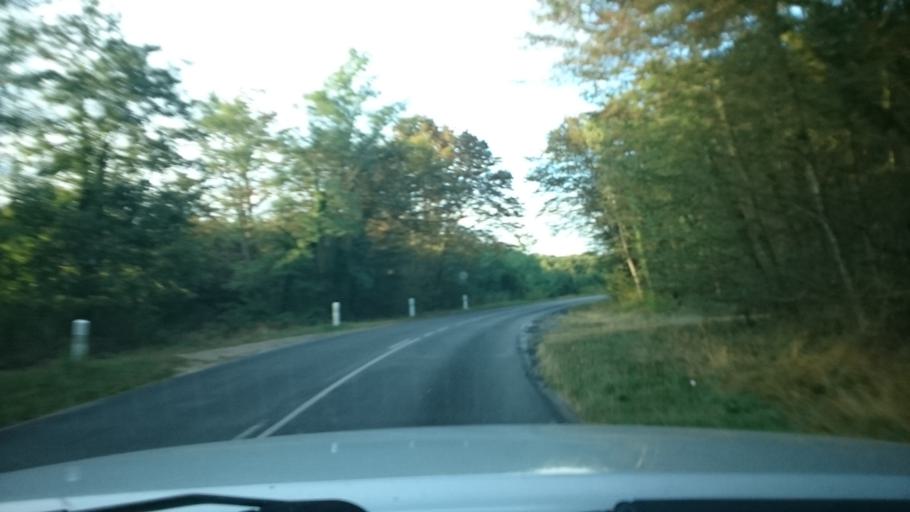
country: FR
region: Ile-de-France
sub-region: Departement de Seine-et-Marne
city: Samois-sur-Seine
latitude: 48.4785
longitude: 2.7439
